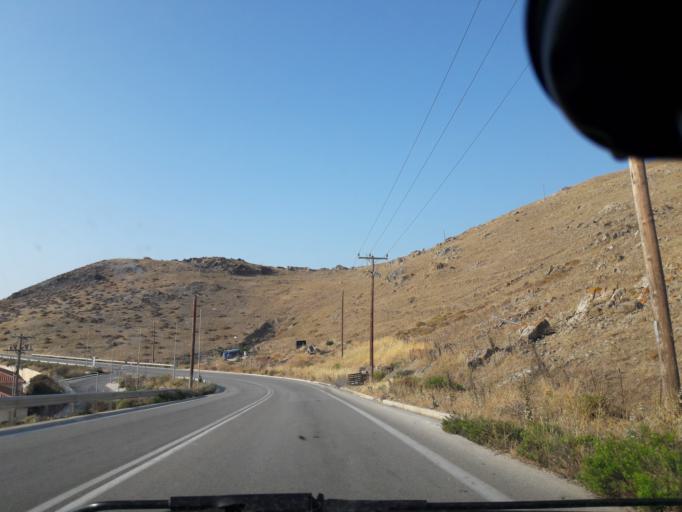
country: GR
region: North Aegean
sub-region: Nomos Lesvou
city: Myrina
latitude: 39.8638
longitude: 25.0561
